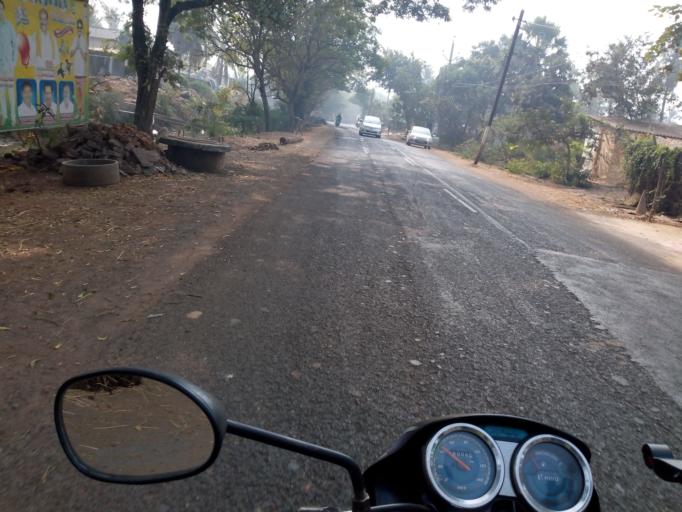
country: IN
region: Andhra Pradesh
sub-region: West Godavari
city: Tadepallegudem
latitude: 16.7795
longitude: 81.4209
